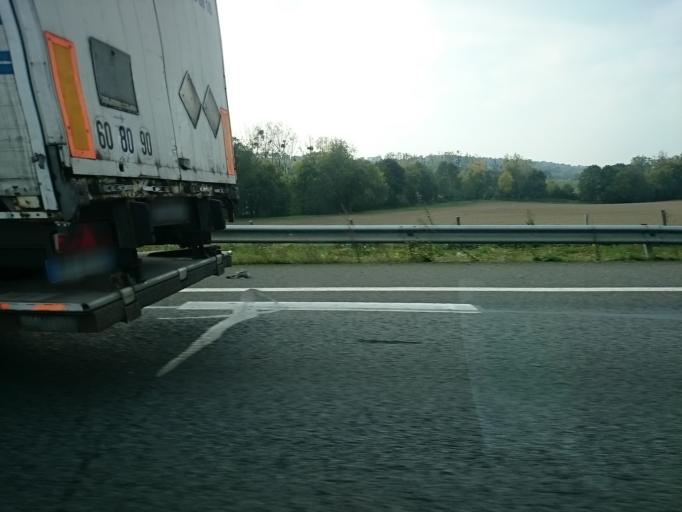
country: FR
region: Brittany
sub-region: Departement d'Ille-et-Vilaine
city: Pance
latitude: 47.8850
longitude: -1.6900
